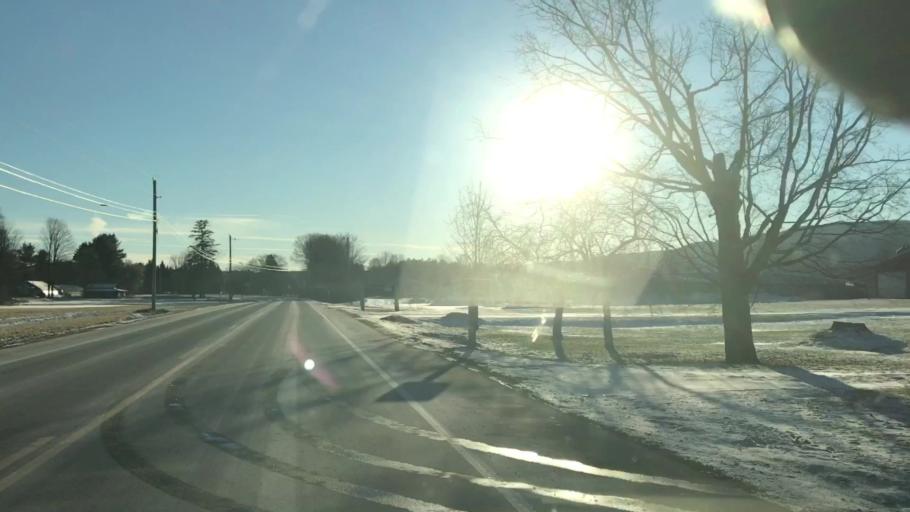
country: US
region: New Hampshire
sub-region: Grafton County
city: Orford
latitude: 43.8823
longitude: -72.1544
